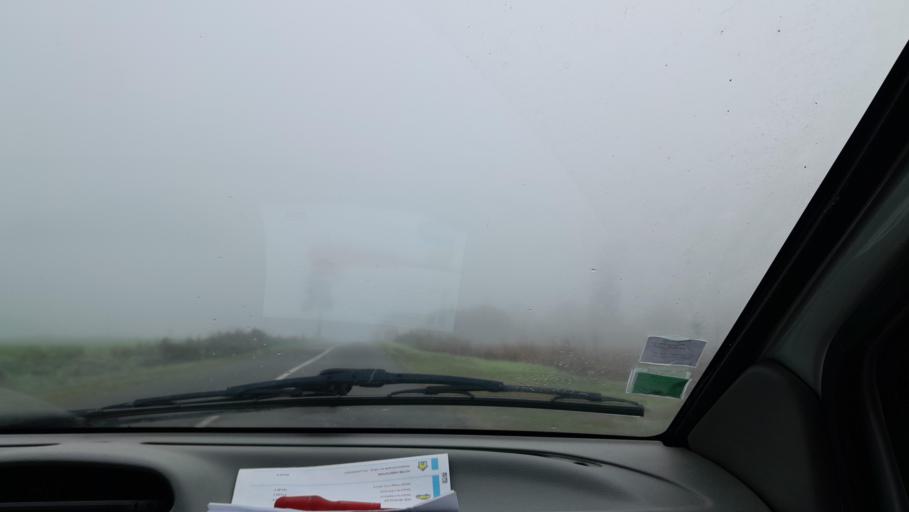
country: FR
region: Brittany
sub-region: Departement d'Ille-et-Vilaine
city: Le Pertre
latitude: 48.0154
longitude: -1.0381
